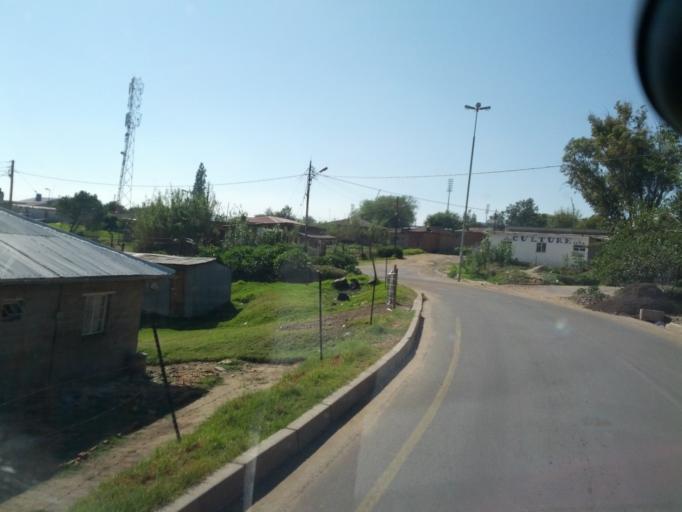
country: LS
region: Maseru
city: Maseru
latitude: -29.3073
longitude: 27.4958
